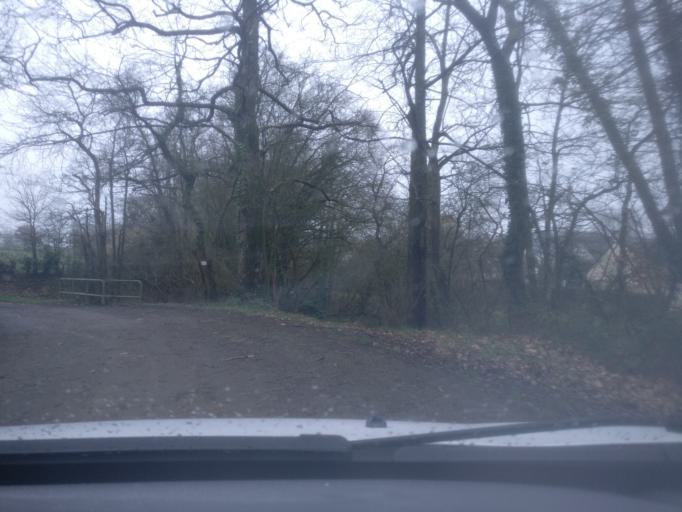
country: FR
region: Brittany
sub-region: Departement d'Ille-et-Vilaine
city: Chasne-sur-Illet
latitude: 48.2947
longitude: -1.5879
